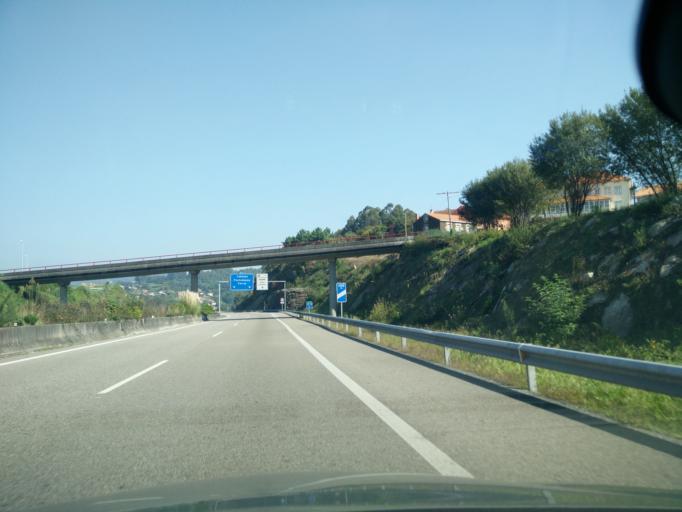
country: ES
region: Galicia
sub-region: Provincia da Coruna
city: Mino
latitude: 43.3464
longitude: -8.2020
